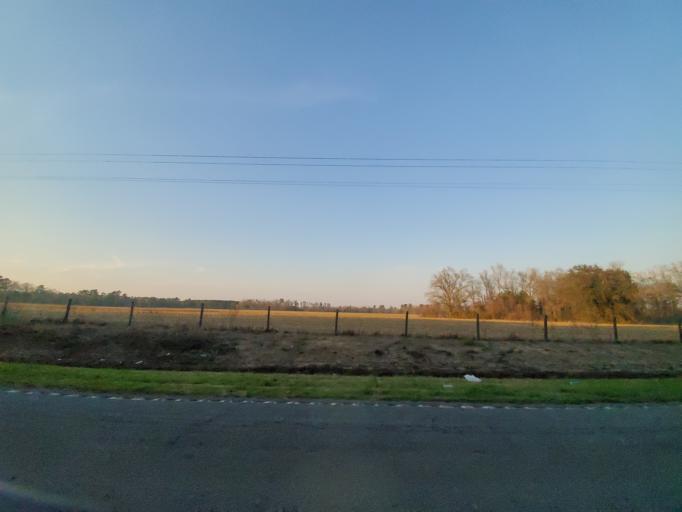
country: US
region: South Carolina
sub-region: Dorchester County
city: Saint George
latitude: 33.0459
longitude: -80.5878
